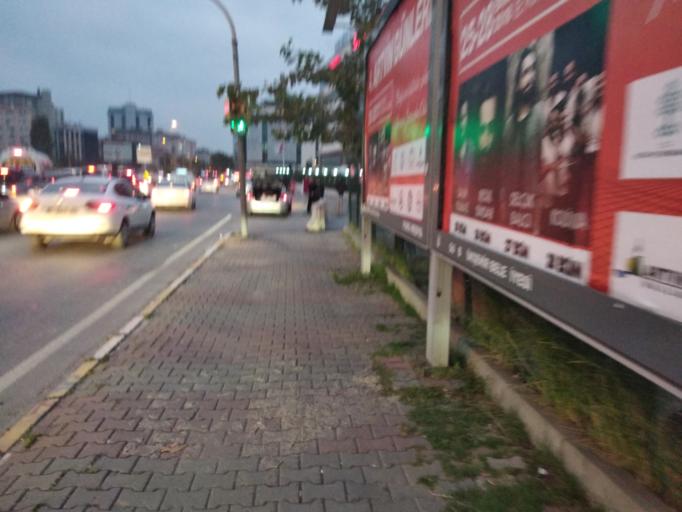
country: TR
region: Istanbul
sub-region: Atasehir
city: Atasehir
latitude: 40.9795
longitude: 29.1263
